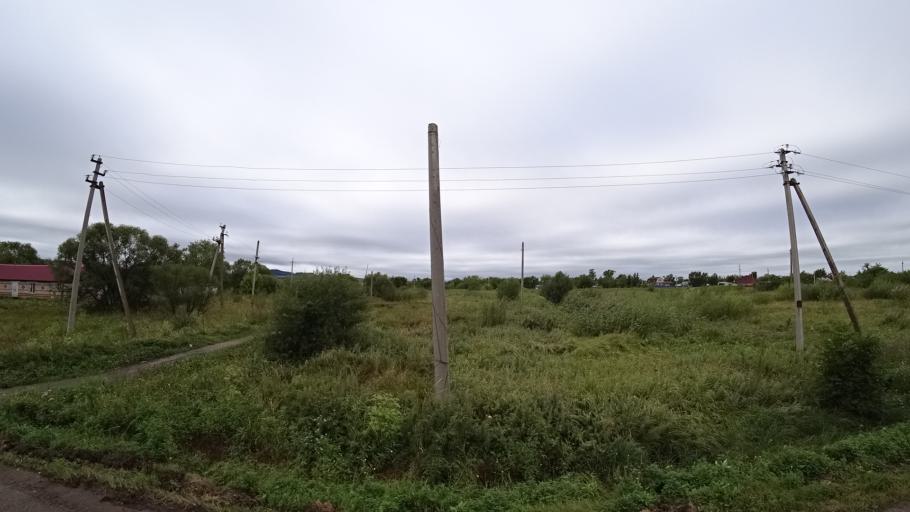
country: RU
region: Primorskiy
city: Monastyrishche
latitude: 44.1951
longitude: 132.4796
